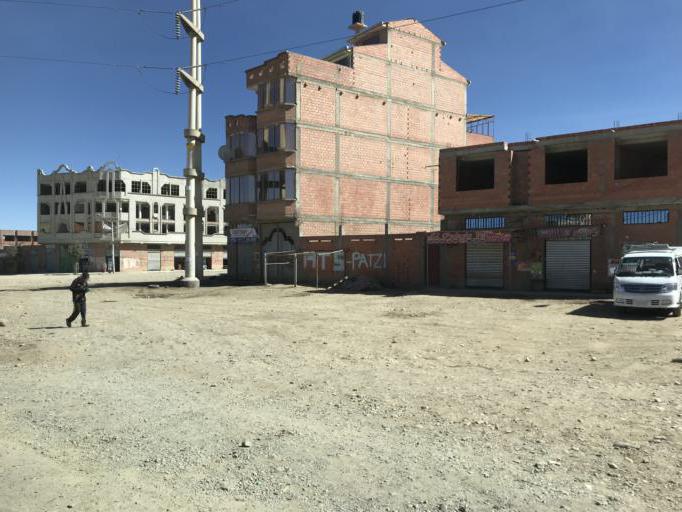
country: BO
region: La Paz
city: La Paz
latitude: -16.5013
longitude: -68.2400
